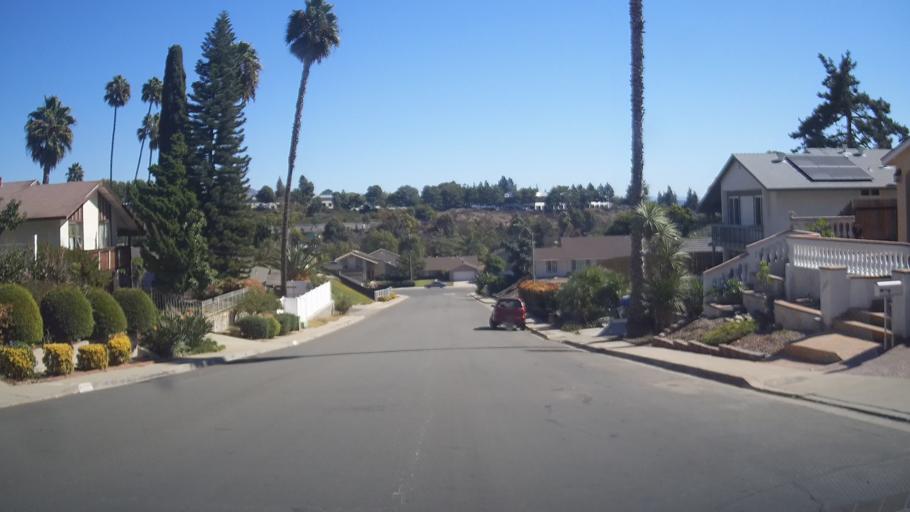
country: US
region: California
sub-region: San Diego County
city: Poway
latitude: 32.9906
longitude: -117.0869
